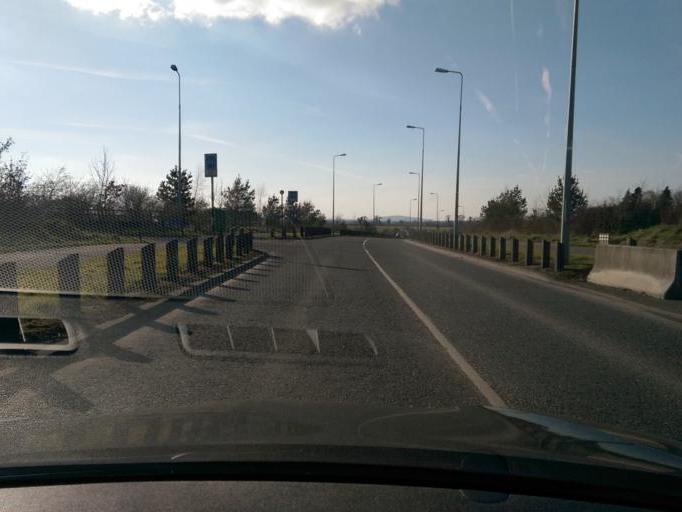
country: IE
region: Leinster
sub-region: Kildare
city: Naas
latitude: 53.2080
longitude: -6.6723
